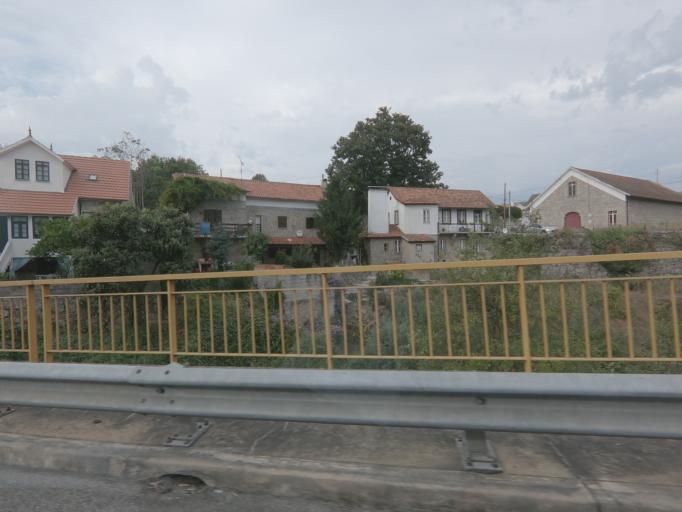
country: PT
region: Viseu
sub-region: Santa Comba Dao
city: Santa Comba Dao
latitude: 40.3884
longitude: -8.1270
